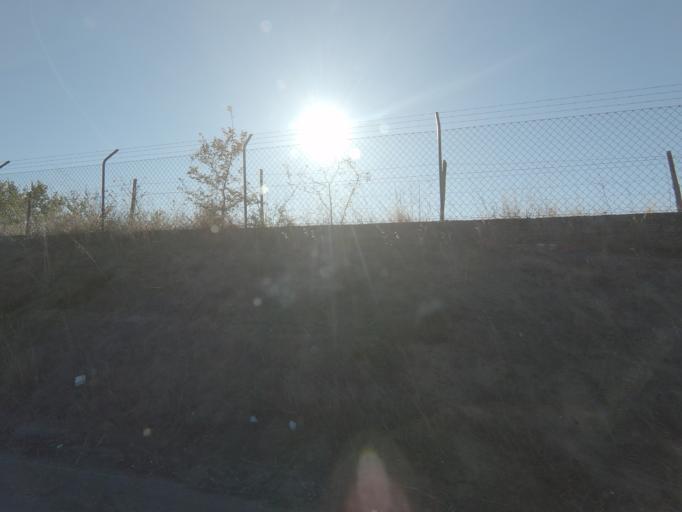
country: PT
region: Setubal
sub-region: Palmela
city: Quinta do Anjo
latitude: 38.5449
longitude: -8.9842
